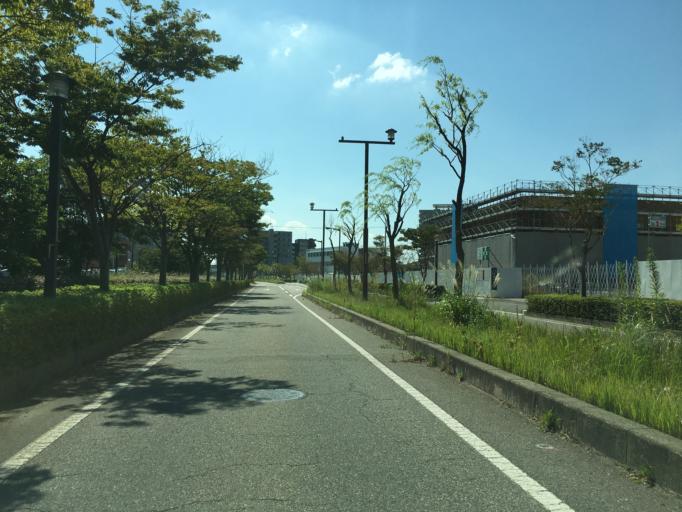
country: JP
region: Niigata
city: Niigata-shi
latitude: 37.8955
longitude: 139.0175
